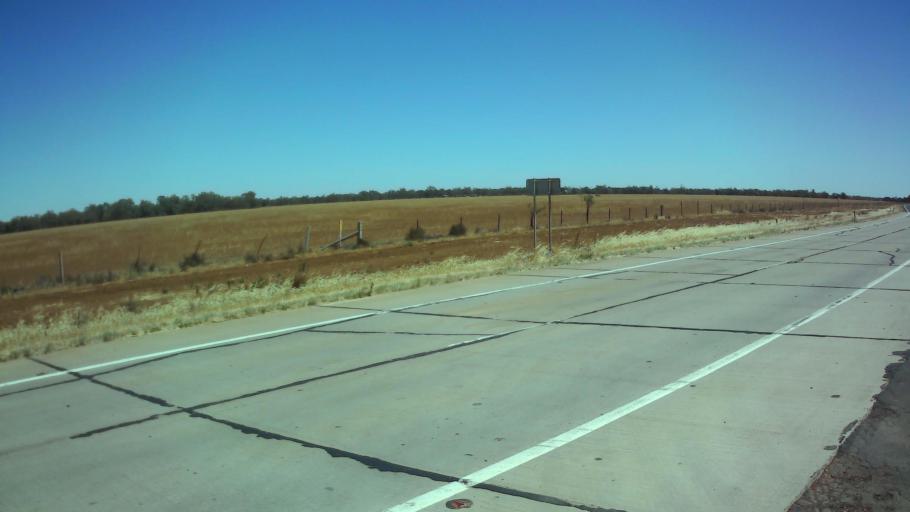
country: AU
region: New South Wales
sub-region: Bland
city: West Wyalong
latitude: -33.7521
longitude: 147.5264
